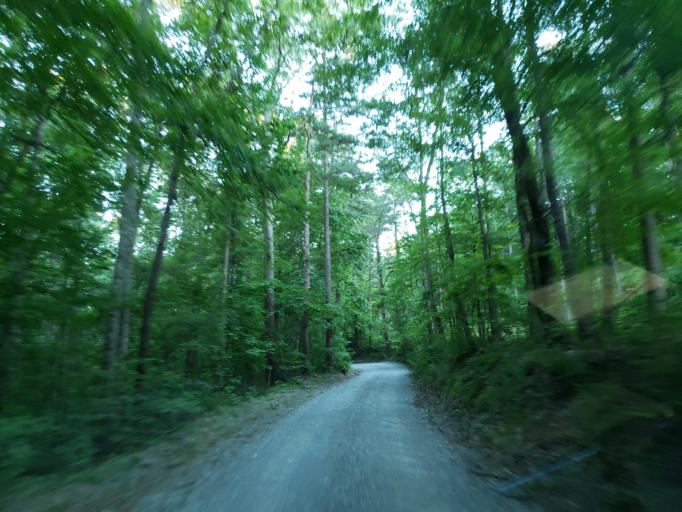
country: US
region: Georgia
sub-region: Bartow County
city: Euharlee
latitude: 34.0906
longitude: -84.8699
